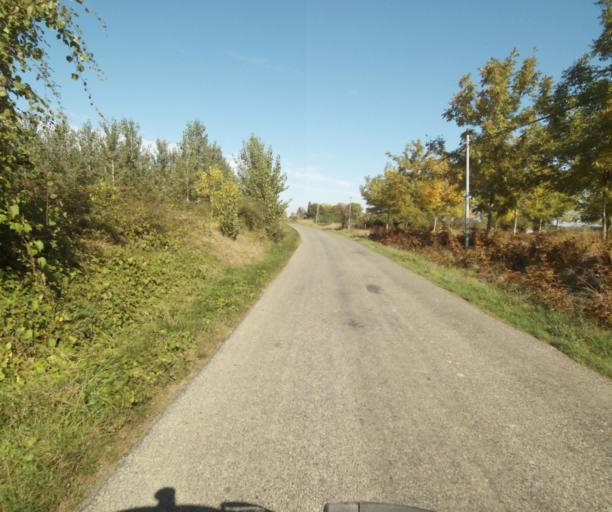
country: FR
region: Midi-Pyrenees
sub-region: Departement du Tarn-et-Garonne
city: Verdun-sur-Garonne
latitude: 43.8649
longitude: 1.2439
